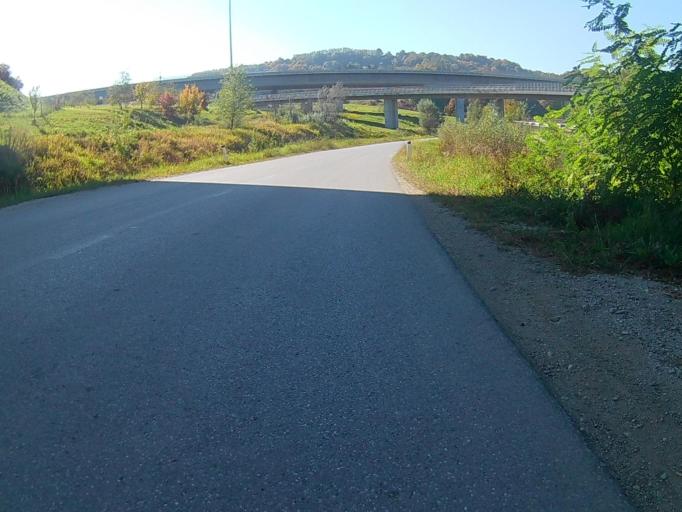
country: SI
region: Pesnica
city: Pesnica pri Mariboru
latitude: 46.5874
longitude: 15.6895
